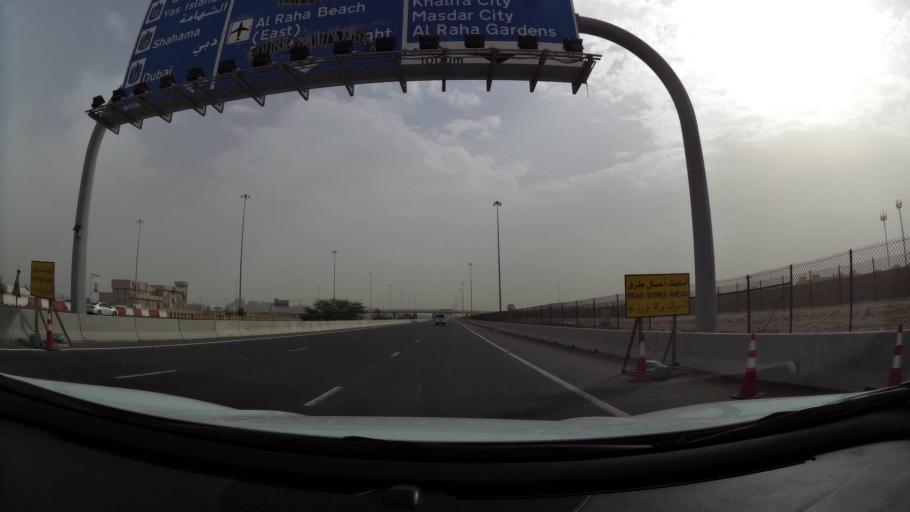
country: AE
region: Abu Dhabi
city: Abu Dhabi
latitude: 24.4415
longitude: 54.5888
